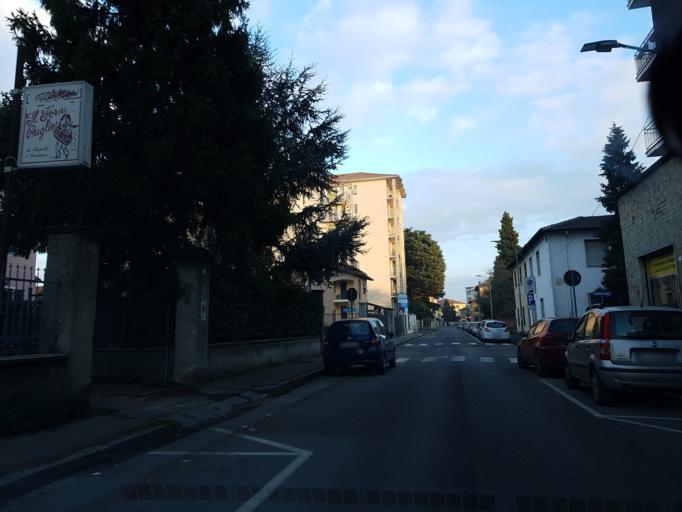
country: IT
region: Piedmont
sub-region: Provincia di Alessandria
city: Novi Ligure
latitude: 44.7642
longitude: 8.7946
